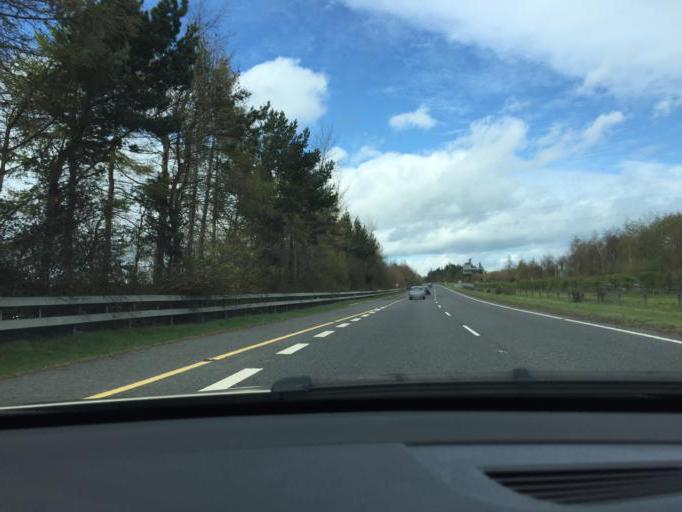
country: IE
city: Kilquade
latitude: 53.0753
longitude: -6.0926
